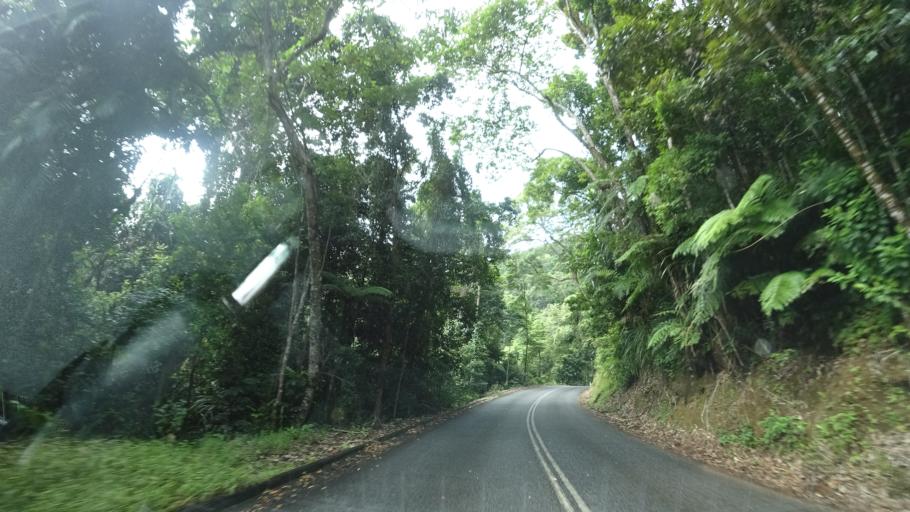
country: AU
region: Queensland
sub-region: Cairns
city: Port Douglas
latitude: -16.2414
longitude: 145.4275
